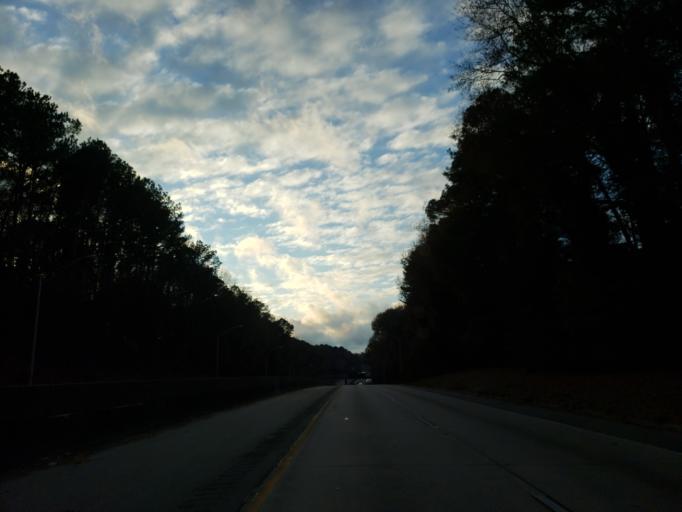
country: US
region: Georgia
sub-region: Fulton County
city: East Point
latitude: 33.6982
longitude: -84.4704
